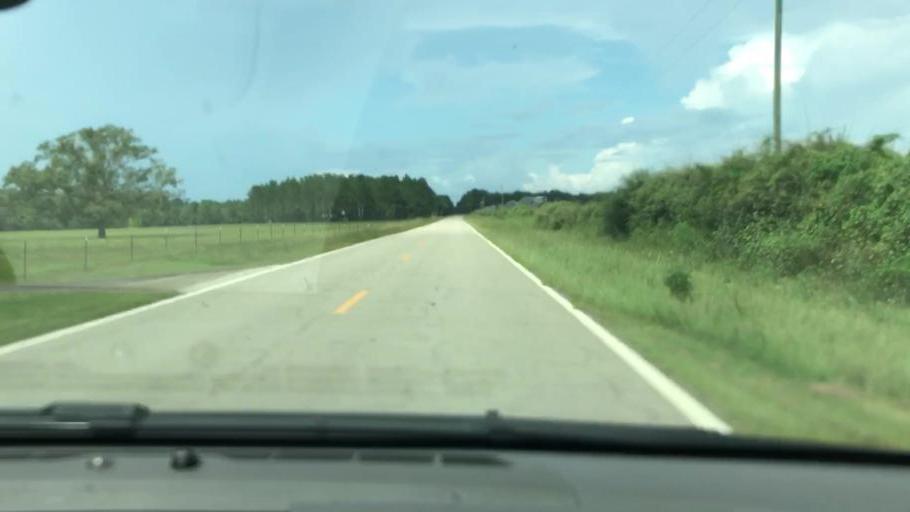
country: US
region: Georgia
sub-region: Seminole County
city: Donalsonville
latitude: 31.1410
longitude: -84.9951
